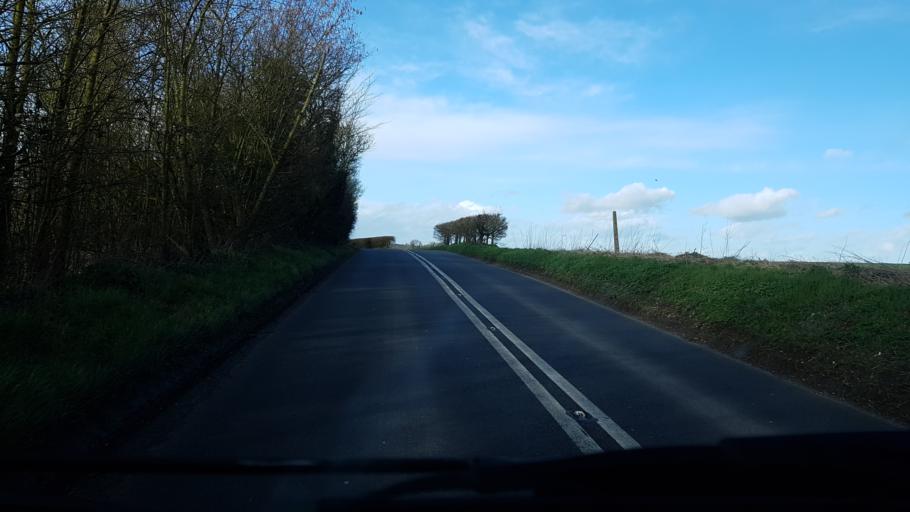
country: GB
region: England
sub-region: Wiltshire
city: Avebury
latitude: 51.4517
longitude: -1.8567
